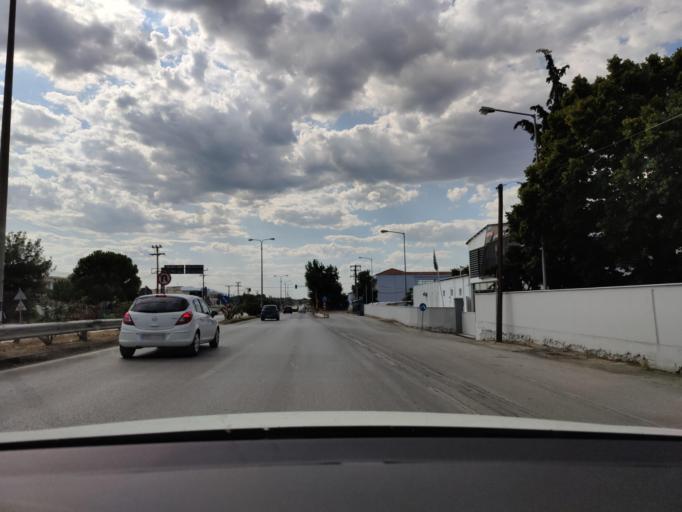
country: GR
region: Central Macedonia
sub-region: Nomos Serron
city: Serres
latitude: 41.0889
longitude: 23.5234
